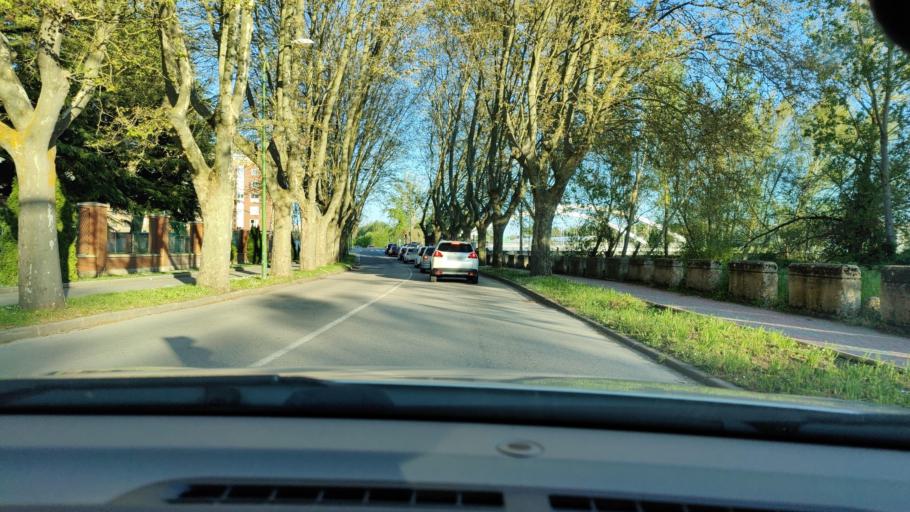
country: ES
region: Castille and Leon
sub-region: Provincia de Burgos
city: Villagonzalo-Pedernales
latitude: 42.3456
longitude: -3.7284
